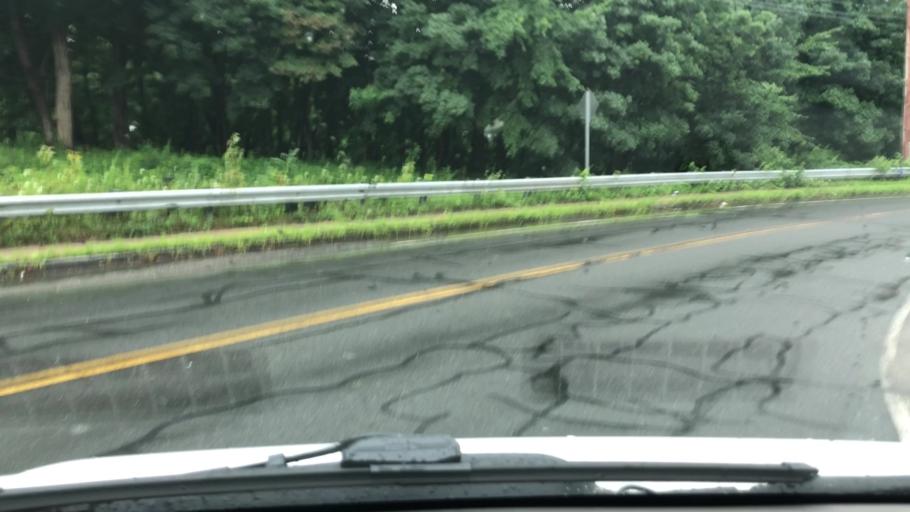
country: US
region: Massachusetts
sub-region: Hampshire County
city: Northampton
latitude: 42.3078
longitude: -72.6456
